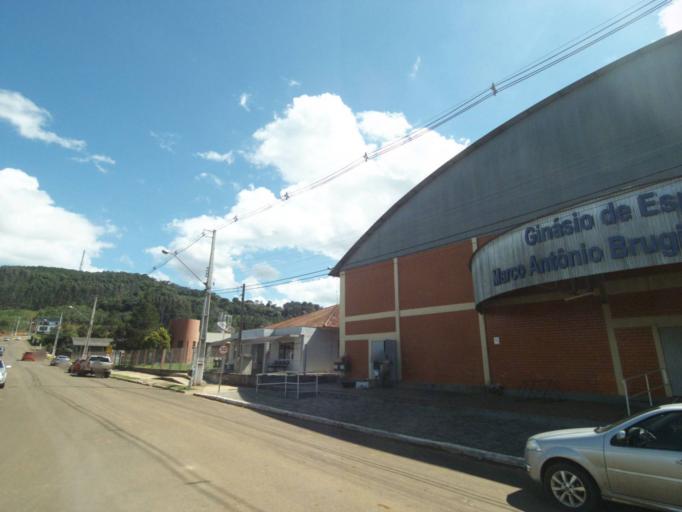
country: BR
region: Parana
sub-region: Uniao Da Vitoria
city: Uniao da Vitoria
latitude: -26.1509
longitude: -51.5479
